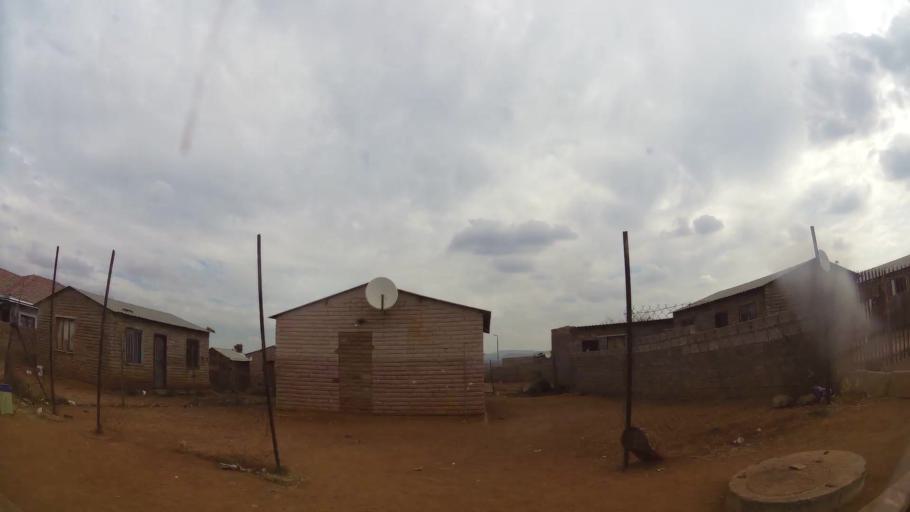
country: ZA
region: Gauteng
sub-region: Ekurhuleni Metropolitan Municipality
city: Germiston
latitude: -26.3843
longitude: 28.1213
